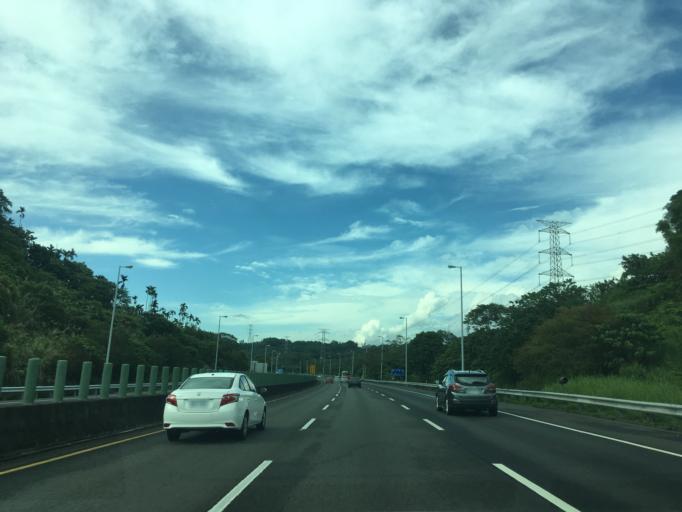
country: TW
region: Taiwan
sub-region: Chiayi
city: Jiayi Shi
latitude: 23.4659
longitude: 120.4980
